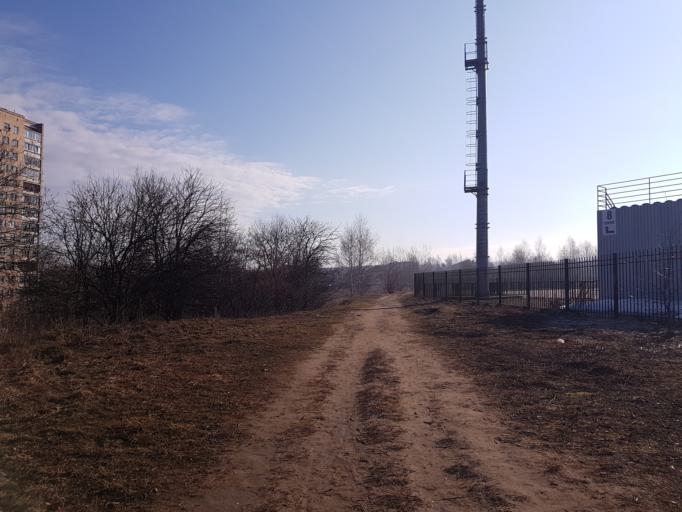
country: RU
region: Moskovskaya
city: Istra
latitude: 55.9073
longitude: 36.8725
